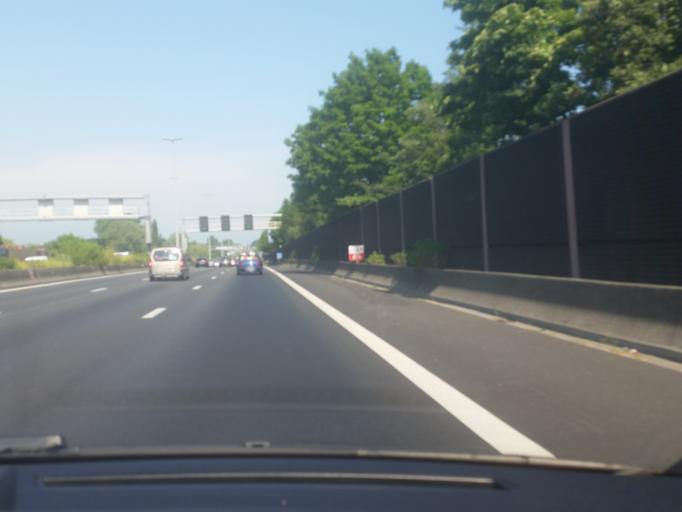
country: BE
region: Flanders
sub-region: Provincie Oost-Vlaanderen
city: Sint-Martens-Latem
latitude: 51.0253
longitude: 3.6700
